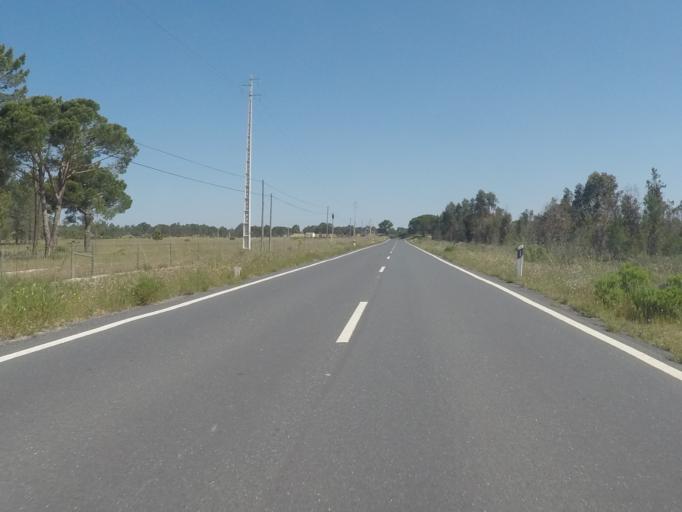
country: PT
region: Setubal
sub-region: Grandola
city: Grandola
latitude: 38.2486
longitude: -8.7374
